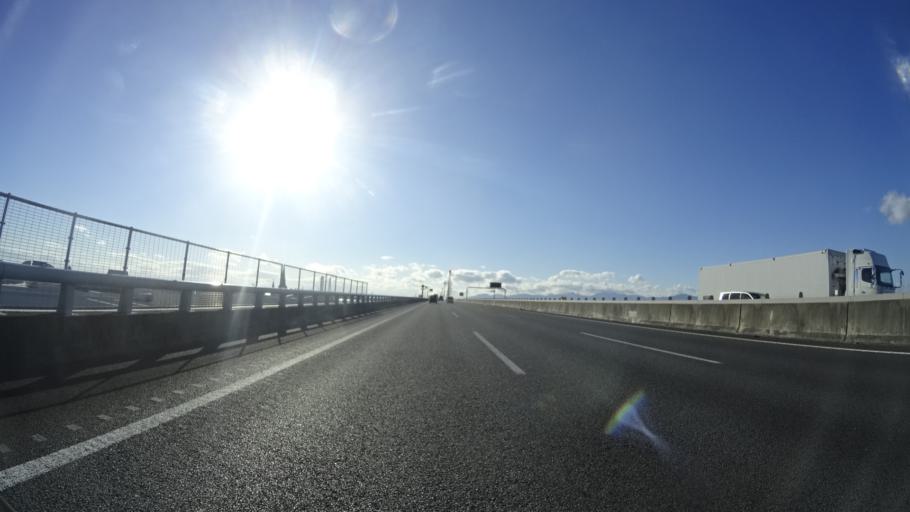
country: JP
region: Aichi
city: Kanie
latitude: 35.0327
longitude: 136.7271
